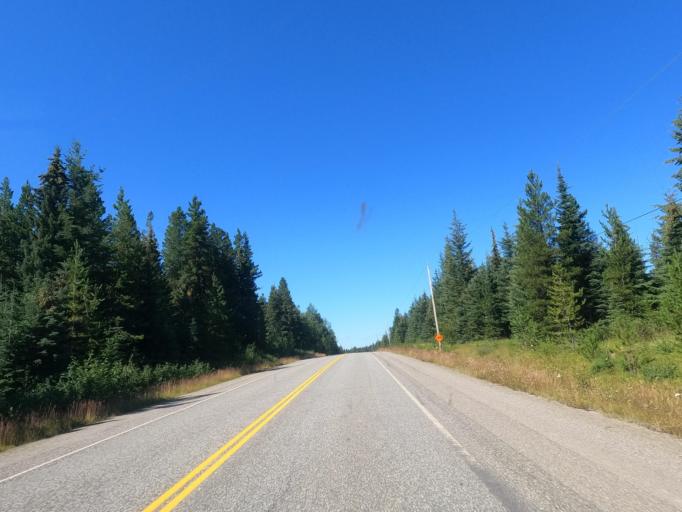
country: CA
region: British Columbia
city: Quesnel
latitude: 53.0275
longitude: -122.0417
